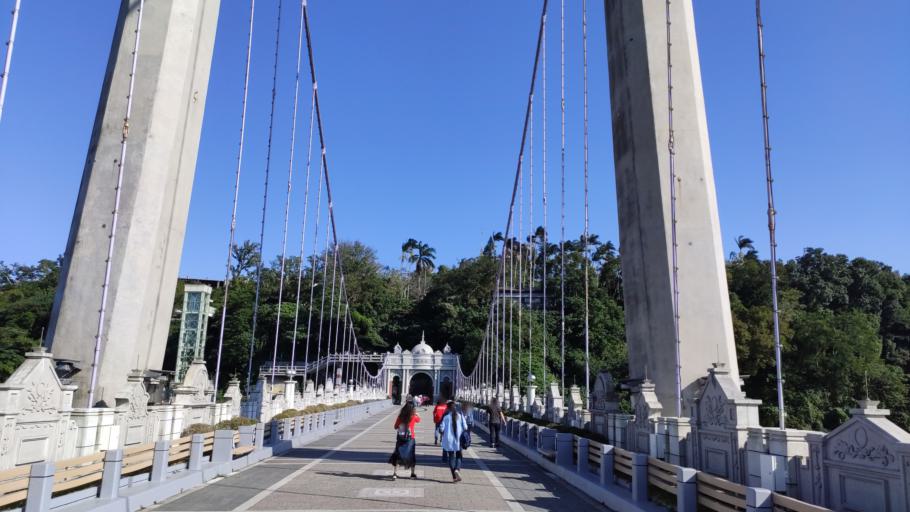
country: TW
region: Taiwan
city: Daxi
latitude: 24.8849
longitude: 121.2833
